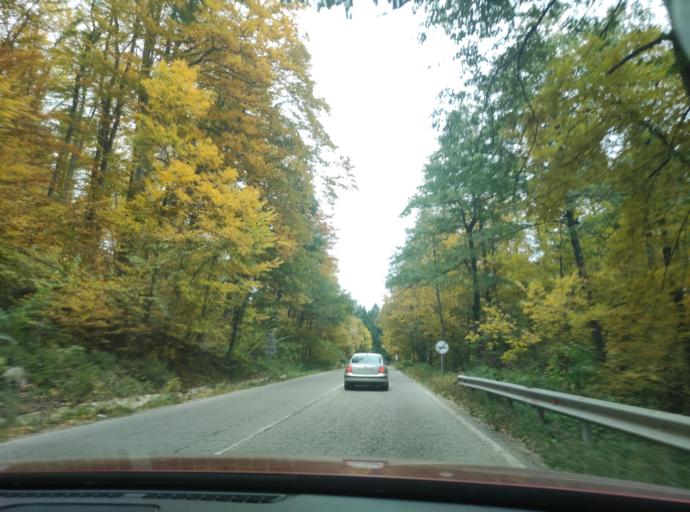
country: BG
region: Montana
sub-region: Obshtina Berkovitsa
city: Berkovitsa
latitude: 43.1782
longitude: 23.1558
